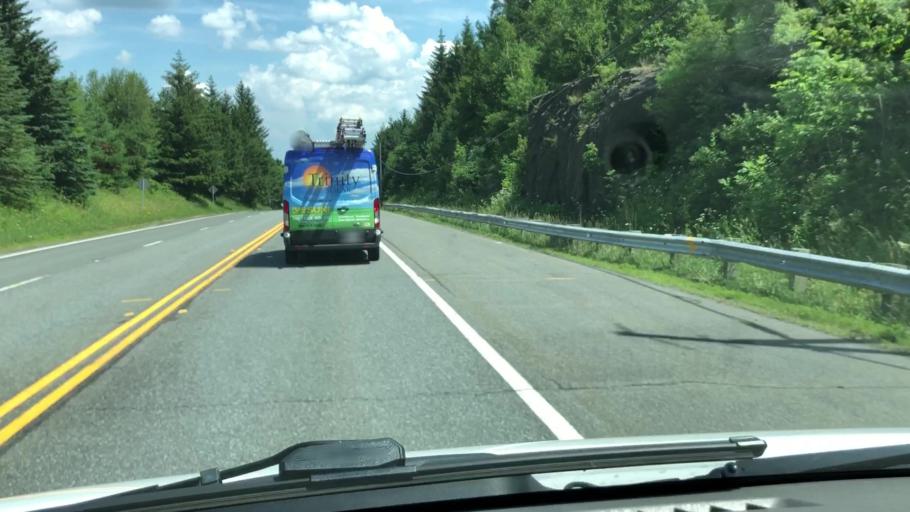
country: US
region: Massachusetts
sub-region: Berkshire County
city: Hinsdale
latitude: 42.4998
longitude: -73.0321
